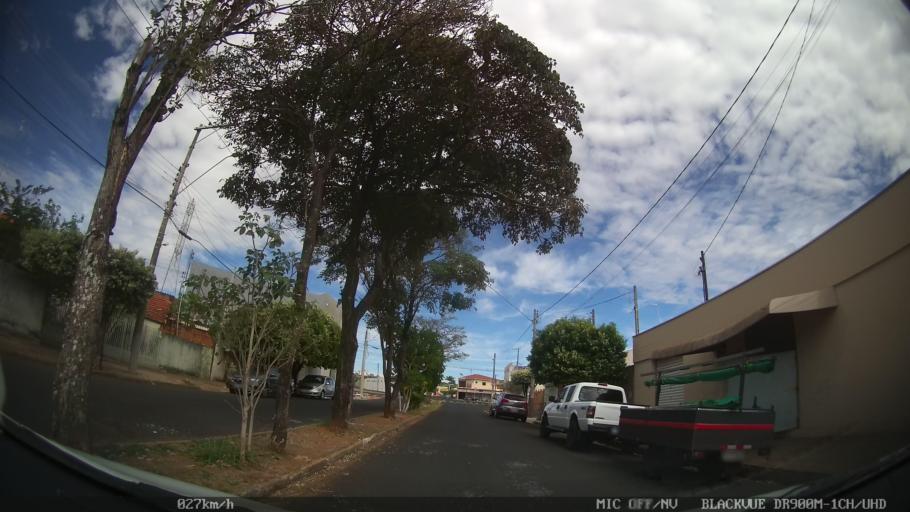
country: BR
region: Sao Paulo
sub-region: Bady Bassitt
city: Bady Bassitt
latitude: -20.8117
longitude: -49.5158
